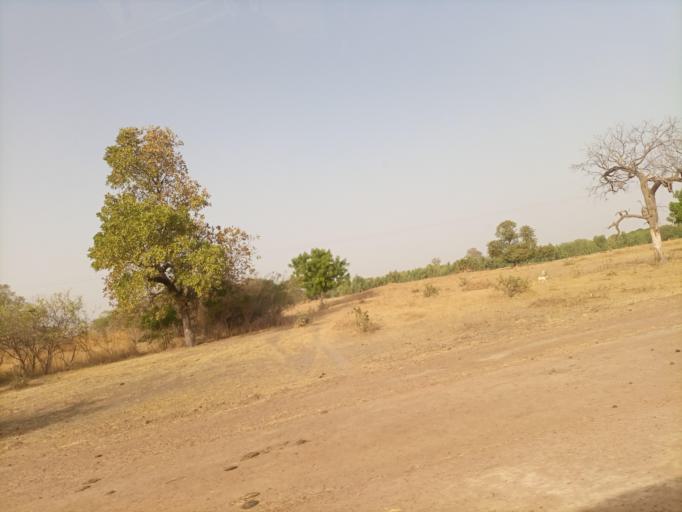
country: SN
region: Fatick
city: Passi
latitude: 14.0226
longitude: -16.2992
